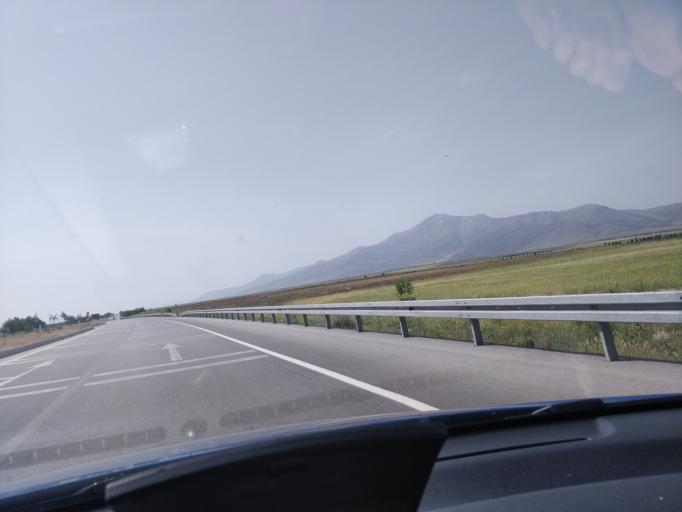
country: TR
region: Konya
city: Guneysinir
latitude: 37.3145
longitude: 32.8533
